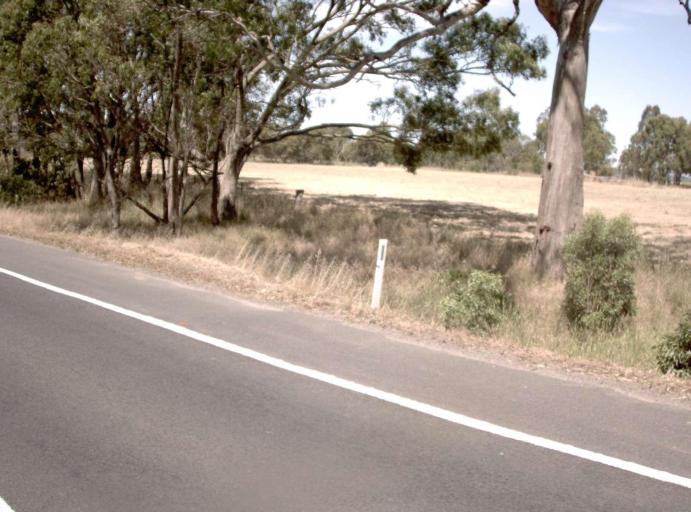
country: AU
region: Victoria
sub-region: Latrobe
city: Traralgon
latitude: -38.1678
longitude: 146.6967
